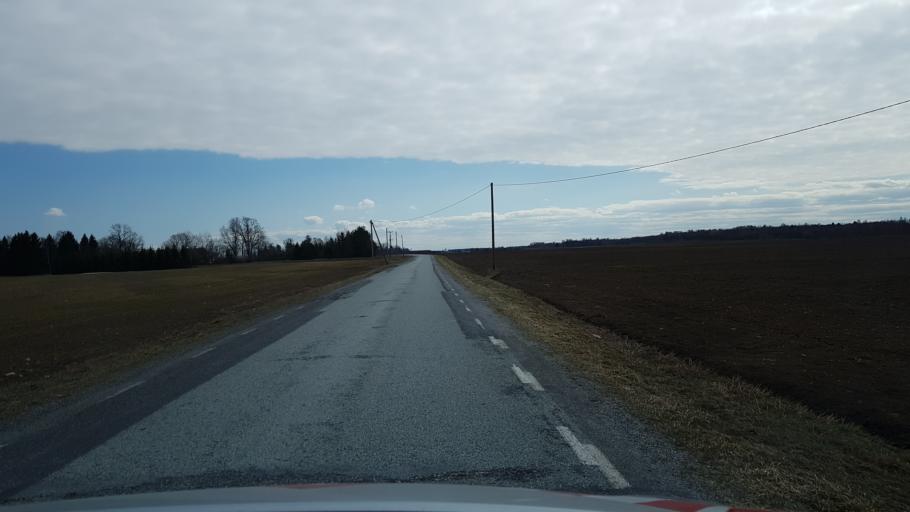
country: EE
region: Laeaene-Virumaa
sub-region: Haljala vald
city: Haljala
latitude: 59.4283
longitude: 26.2143
